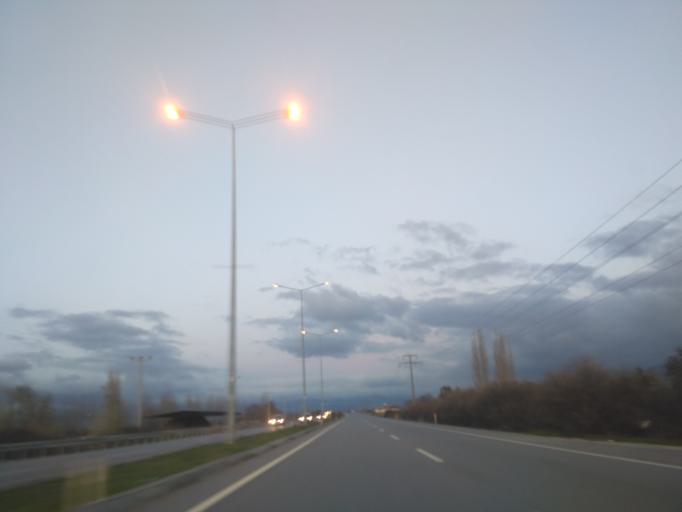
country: TR
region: Balikesir
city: Burhaniye
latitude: 39.5183
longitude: 26.9879
